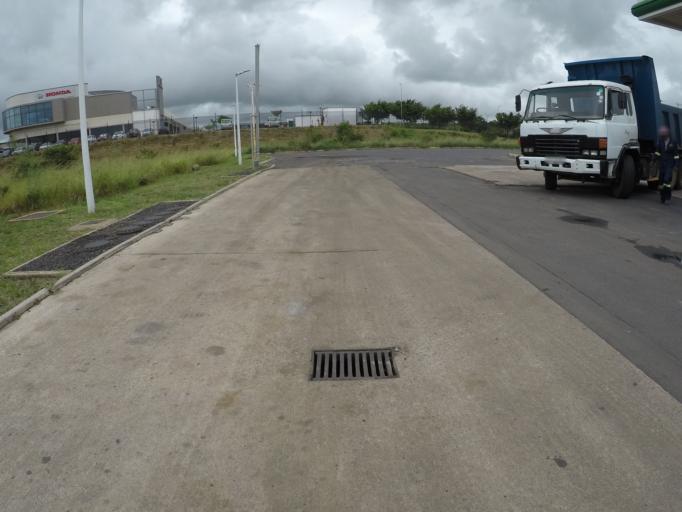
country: ZA
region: KwaZulu-Natal
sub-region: uThungulu District Municipality
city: Empangeni
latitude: -28.7697
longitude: 31.9381
